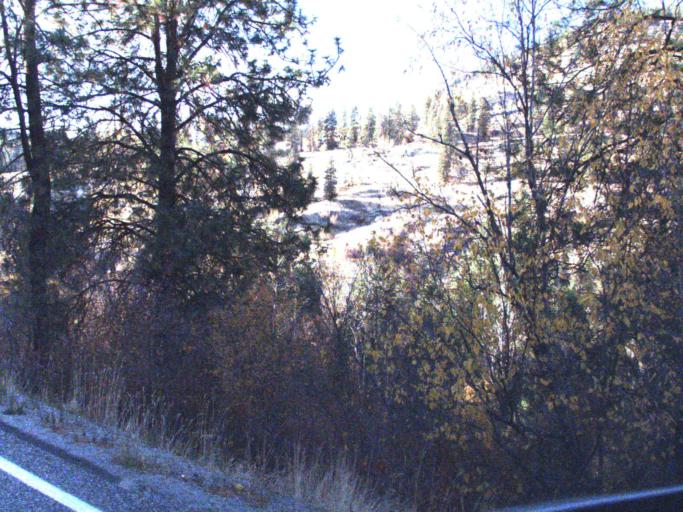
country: CA
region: British Columbia
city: Rossland
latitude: 48.8741
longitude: -117.8507
